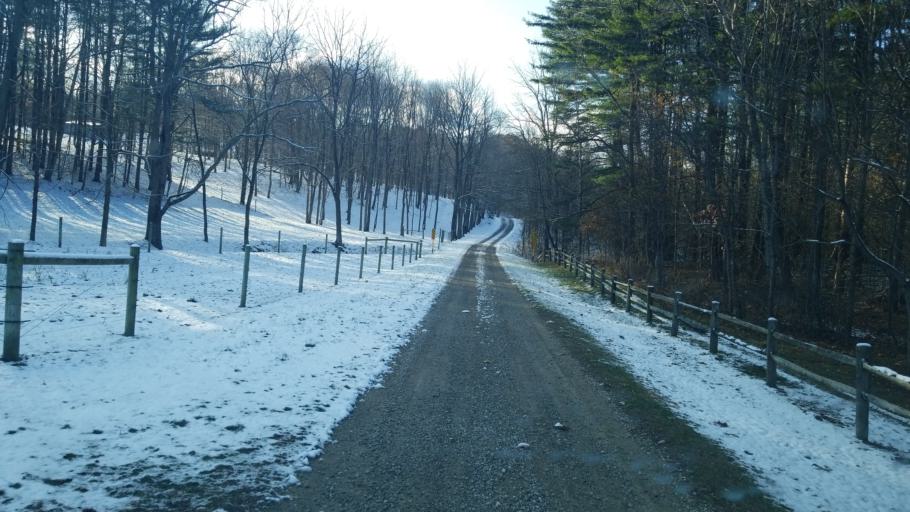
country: US
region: Ohio
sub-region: Licking County
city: Newark
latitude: 40.1535
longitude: -82.3889
